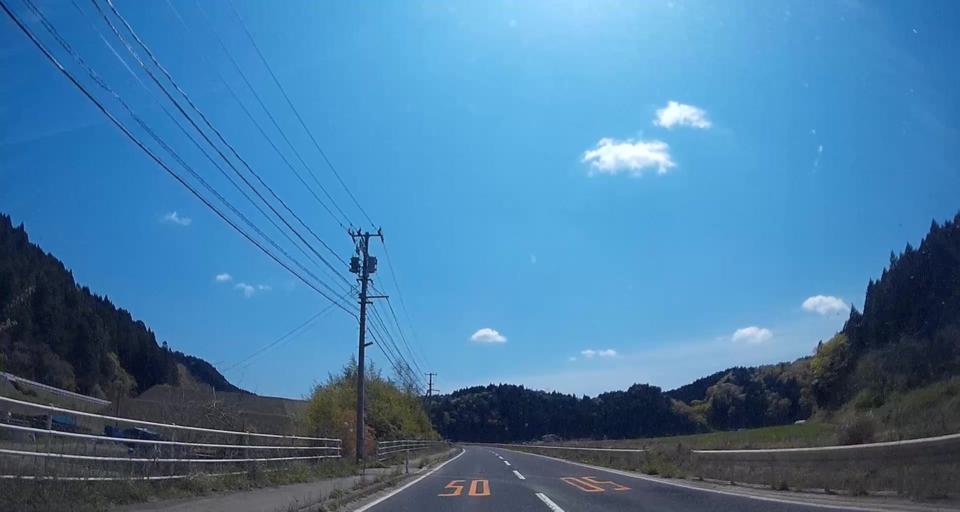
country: JP
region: Miyagi
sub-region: Oshika Gun
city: Onagawa Cho
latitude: 38.6474
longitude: 141.4246
